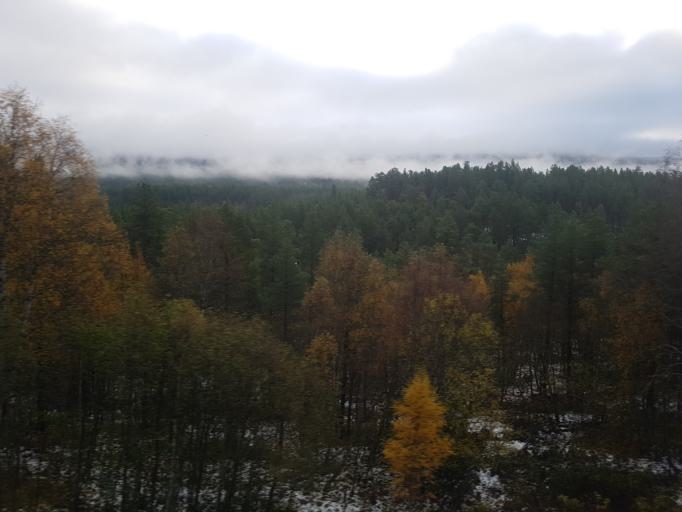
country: NO
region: Sor-Trondelag
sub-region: Oppdal
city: Oppdal
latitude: 62.6440
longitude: 9.8264
